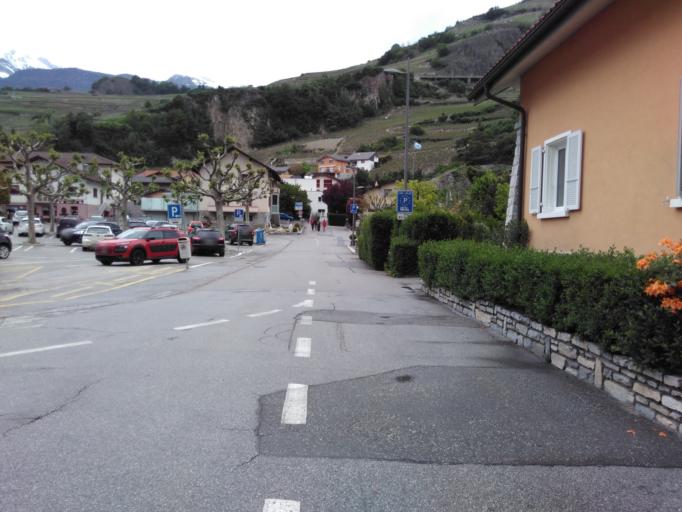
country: CH
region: Valais
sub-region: Sion District
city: Saint-Leonard
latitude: 46.2550
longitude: 7.4259
